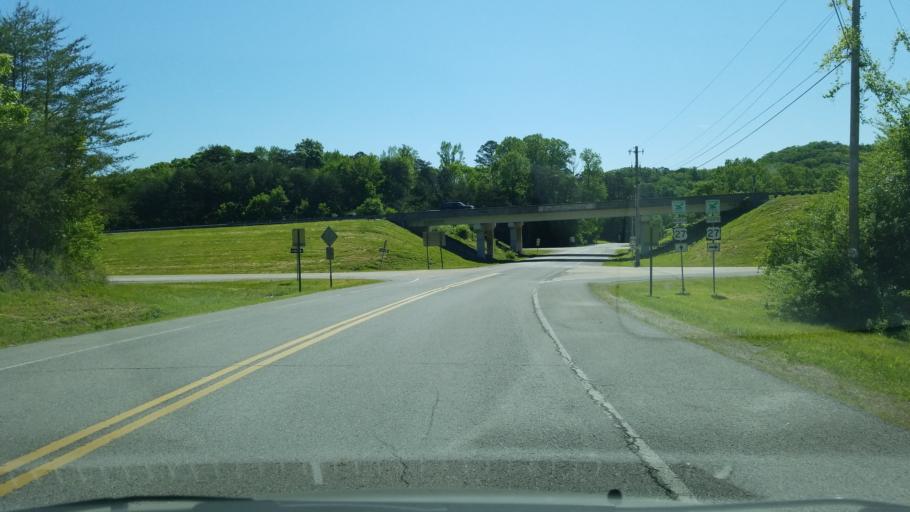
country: US
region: Tennessee
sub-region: Hamilton County
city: Walden
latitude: 35.1580
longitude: -85.2865
